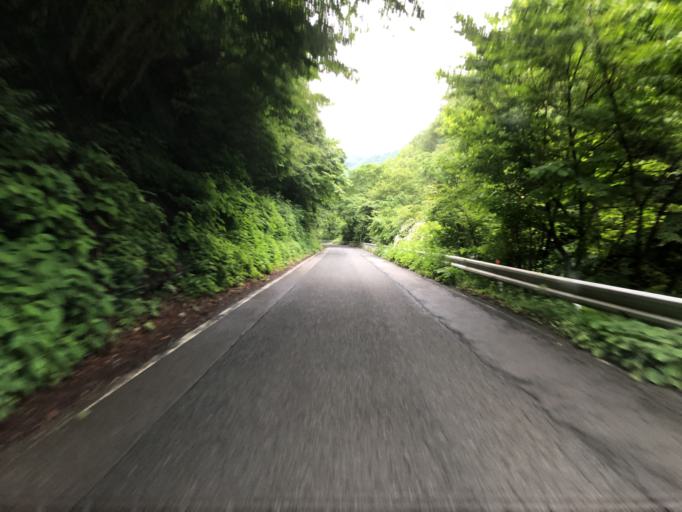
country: JP
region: Fukushima
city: Namie
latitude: 37.6811
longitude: 140.8633
